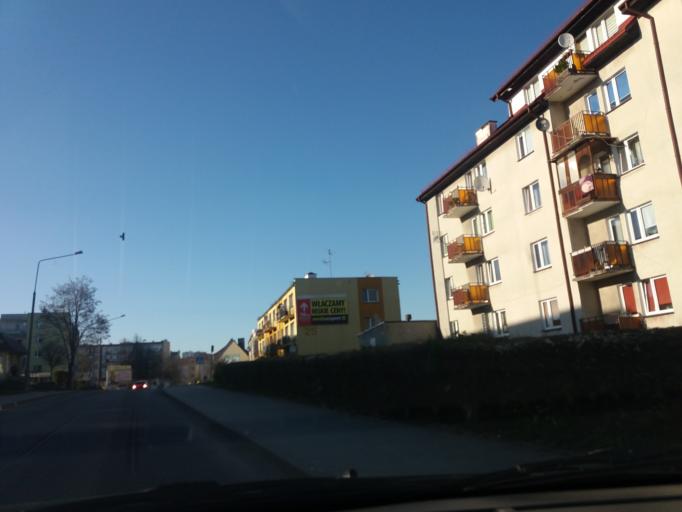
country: PL
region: Warmian-Masurian Voivodeship
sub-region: Powiat nidzicki
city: Nidzica
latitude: 53.3550
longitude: 20.4267
